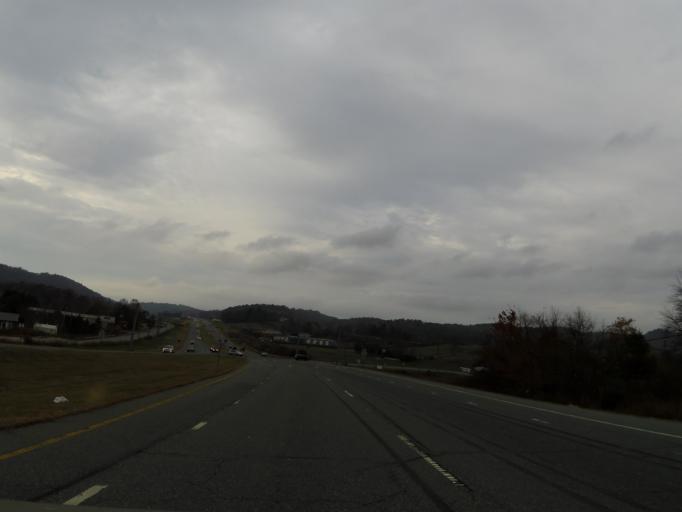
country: US
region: North Carolina
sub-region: Watauga County
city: Boone
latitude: 36.2359
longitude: -81.5076
